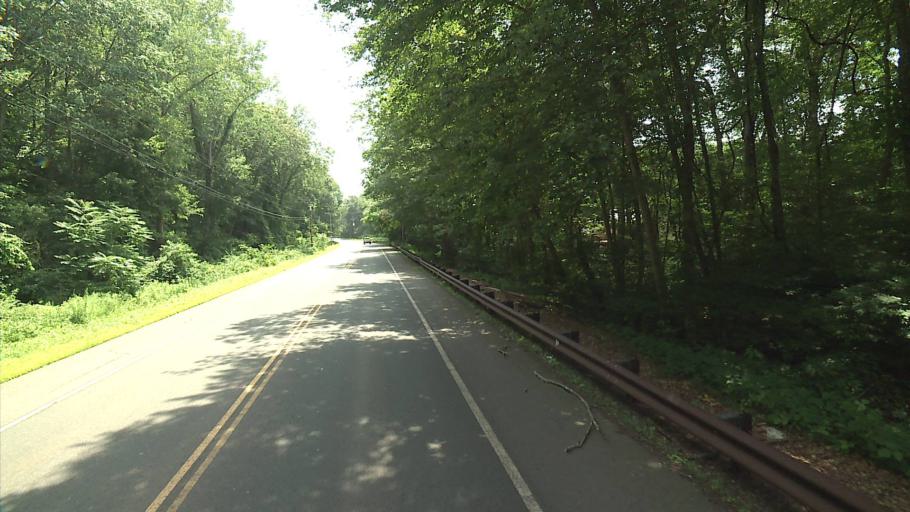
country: US
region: Connecticut
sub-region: New Haven County
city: Madison
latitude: 41.2997
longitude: -72.5838
